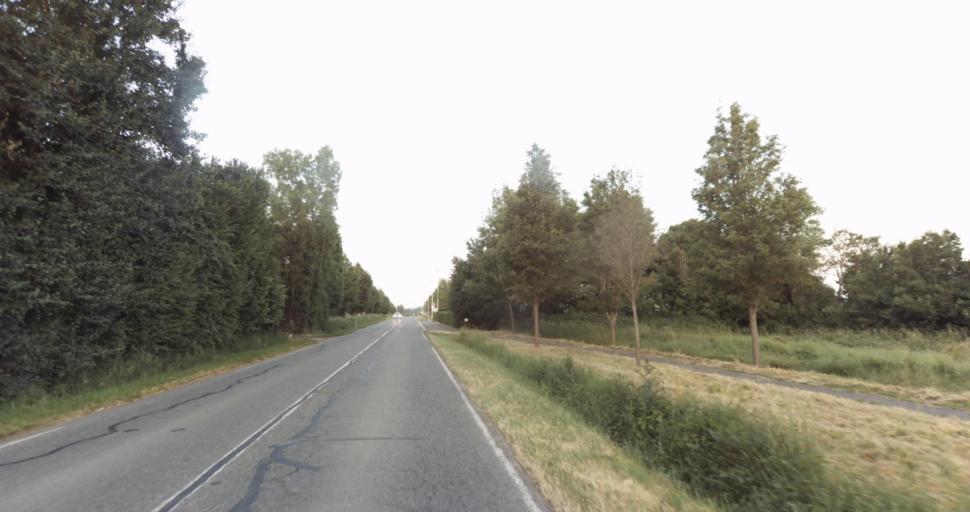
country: FR
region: Midi-Pyrenees
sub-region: Departement de la Haute-Garonne
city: Levignac
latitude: 43.6446
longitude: 1.1629
